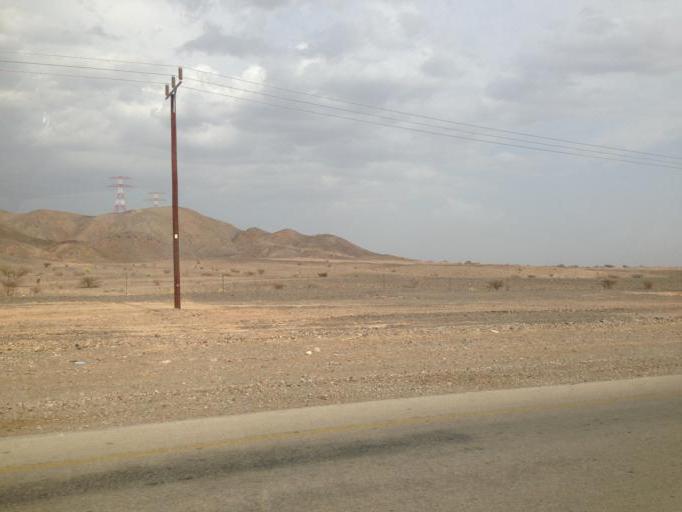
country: OM
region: Ash Sharqiyah
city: Badiyah
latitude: 22.5188
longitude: 58.9485
